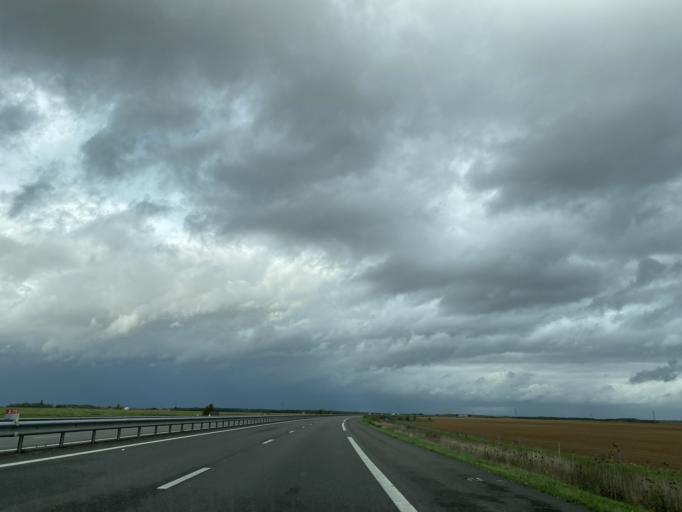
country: FR
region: Centre
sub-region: Departement du Cher
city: Levet
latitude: 46.9503
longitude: 2.4165
